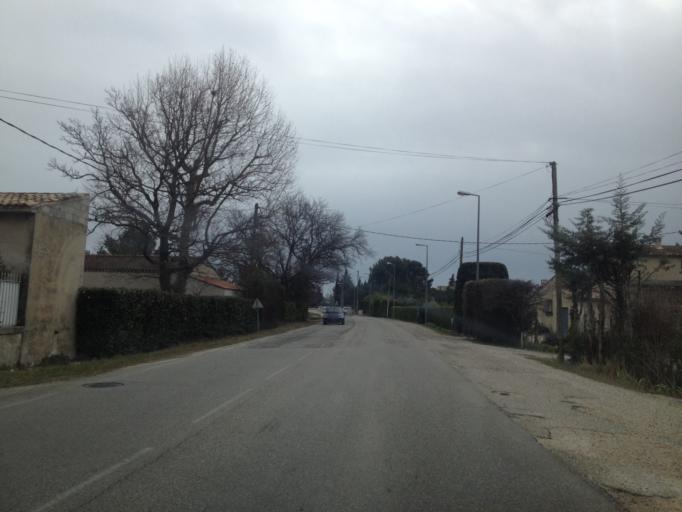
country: FR
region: Provence-Alpes-Cote d'Azur
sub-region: Departement du Vaucluse
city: Jonquieres
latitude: 44.1247
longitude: 4.8980
